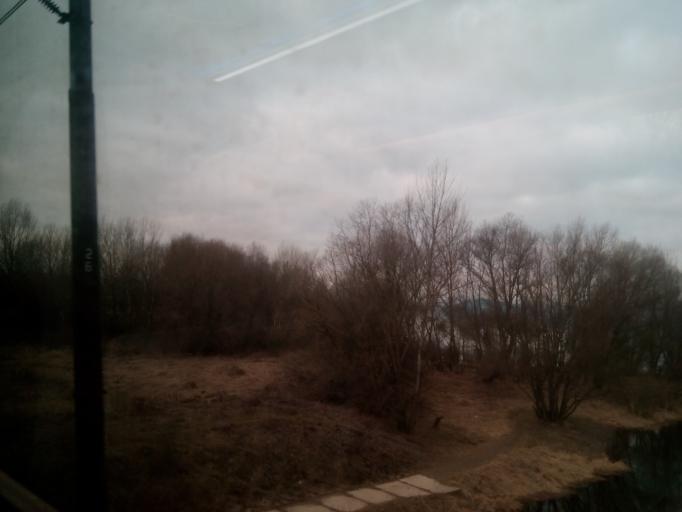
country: SK
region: Zilinsky
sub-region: Okres Liptovsky Mikulas
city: Liptovsky Mikulas
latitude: 49.0918
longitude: 19.5862
